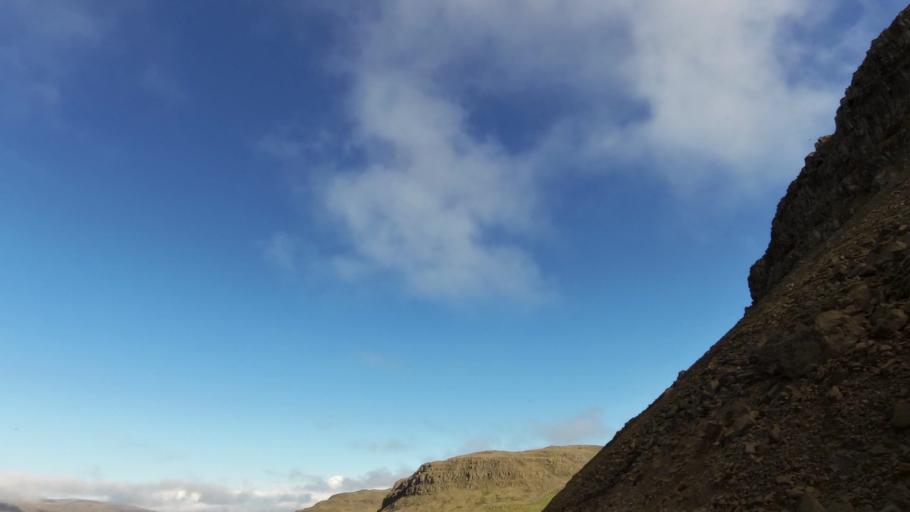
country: IS
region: West
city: Olafsvik
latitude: 65.5653
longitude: -24.0413
